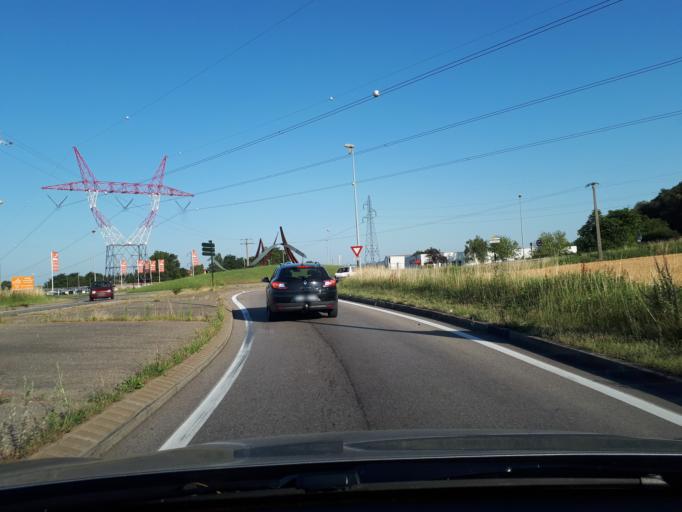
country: FR
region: Rhone-Alpes
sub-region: Departement de l'Isere
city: Grenay
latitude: 45.6728
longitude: 5.0799
